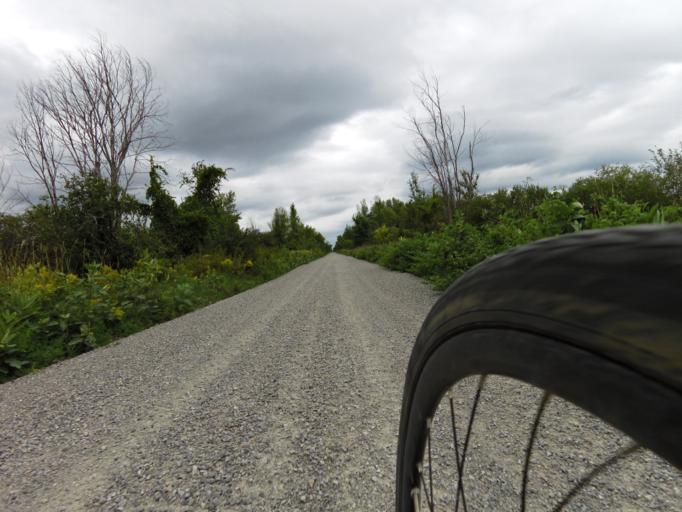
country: CA
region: Ontario
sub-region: Lanark County
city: Smiths Falls
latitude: 44.9271
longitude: -76.0326
